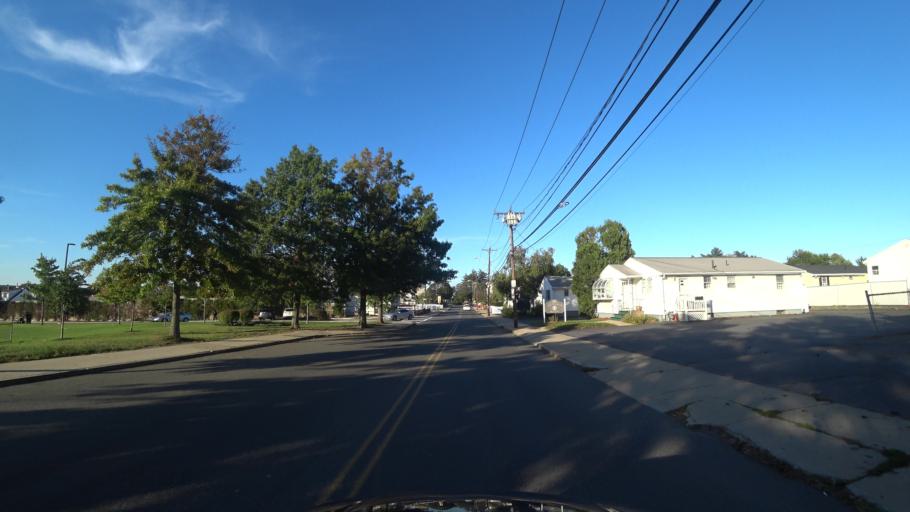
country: US
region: Massachusetts
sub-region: Suffolk County
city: Revere
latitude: 42.4196
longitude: -71.0183
